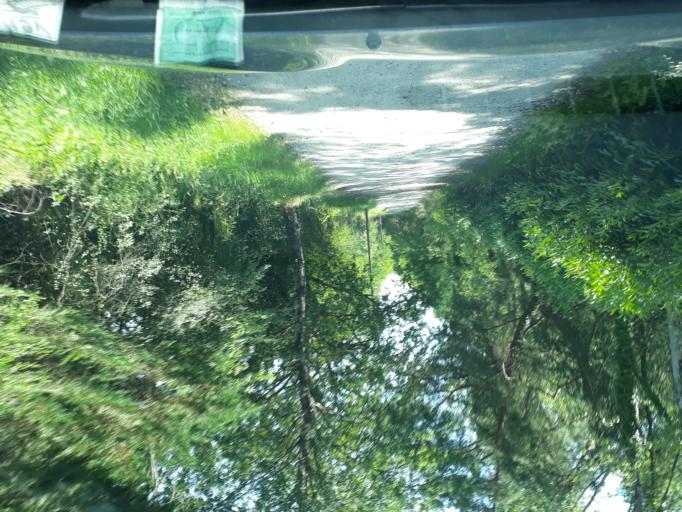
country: FR
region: Centre
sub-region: Departement du Loir-et-Cher
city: Vouzon
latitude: 47.6357
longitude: 2.0503
